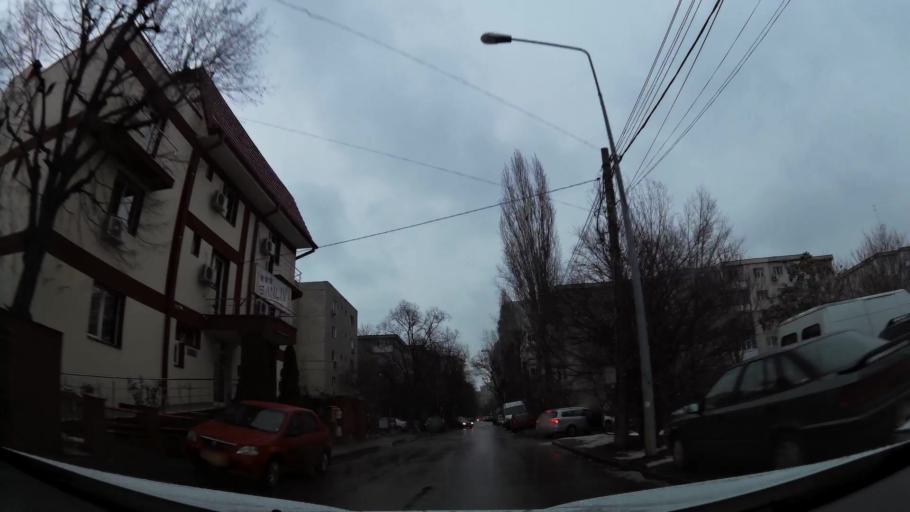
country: RO
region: Ilfov
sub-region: Comuna Chiajna
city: Rosu
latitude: 44.4304
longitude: 26.0130
